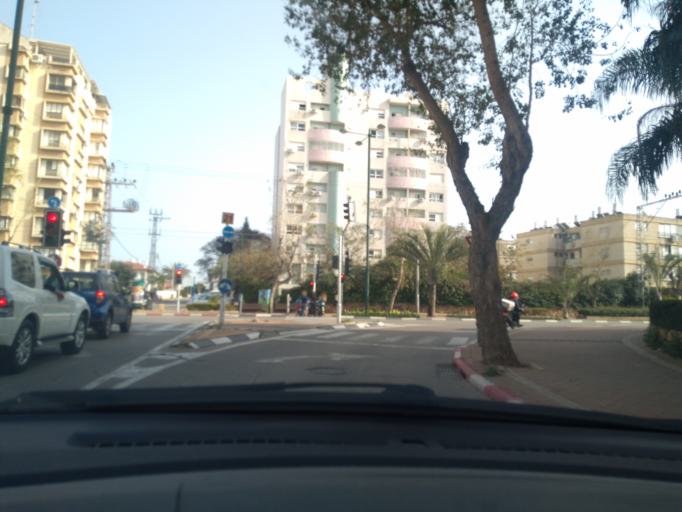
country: IL
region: Central District
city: Netanya
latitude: 32.3313
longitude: 34.8624
